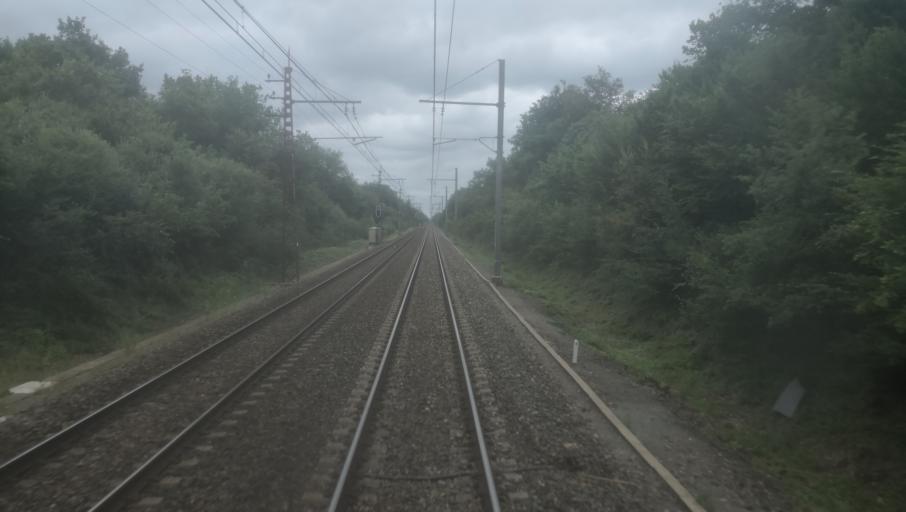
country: FR
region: Midi-Pyrenees
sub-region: Departement du Tarn-et-Garonne
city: Montech
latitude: 43.9413
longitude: 1.2764
